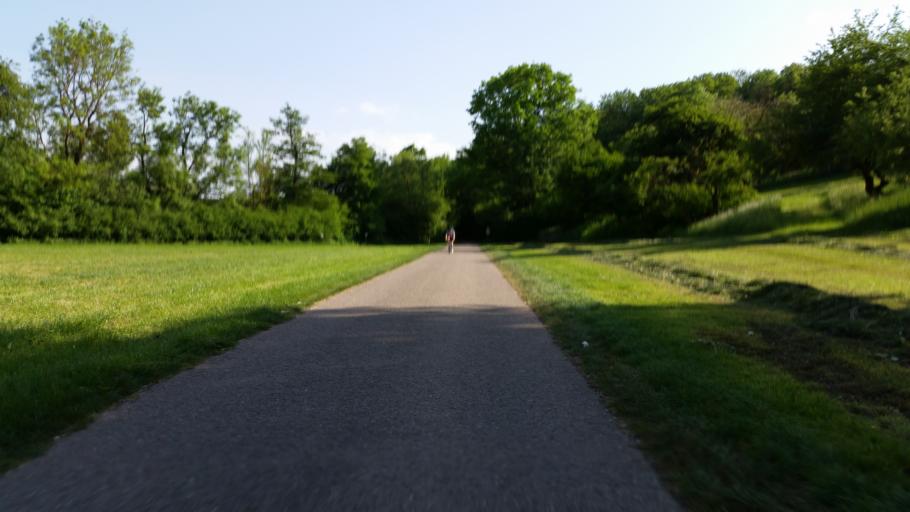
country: DE
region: Baden-Wuerttemberg
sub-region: Regierungsbezirk Stuttgart
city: Pleidelsheim
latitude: 48.9472
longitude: 9.1831
